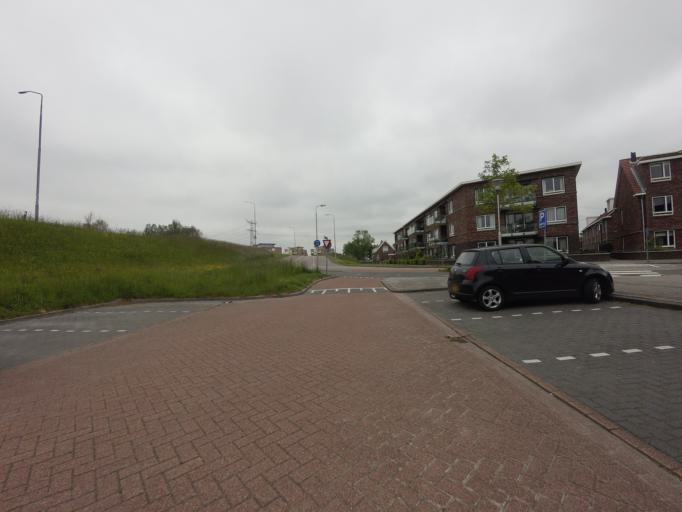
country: NL
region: South Holland
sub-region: Gemeente Spijkenisse
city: Spijkenisse
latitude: 51.8139
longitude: 4.3381
